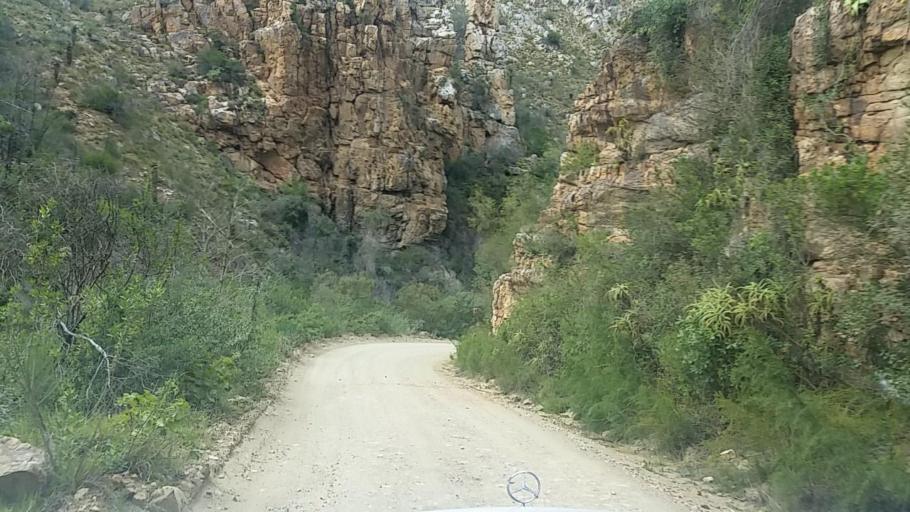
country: ZA
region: Western Cape
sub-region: Eden District Municipality
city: Knysna
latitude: -33.8083
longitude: 23.1797
